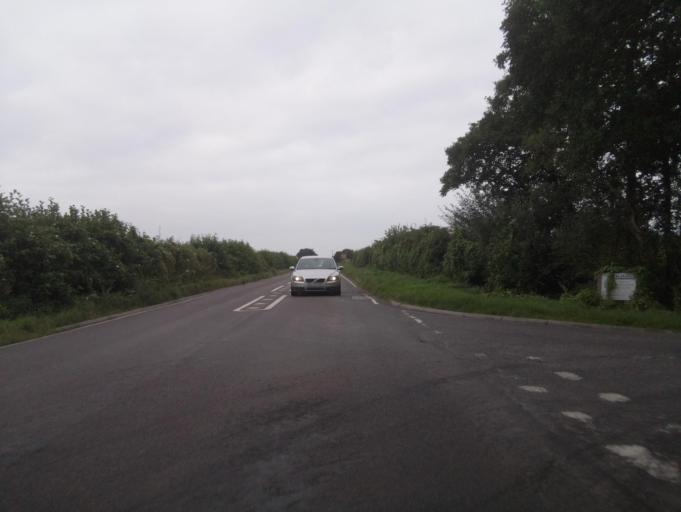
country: GB
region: England
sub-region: Shropshire
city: Shawbury
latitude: 52.8050
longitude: -2.6206
